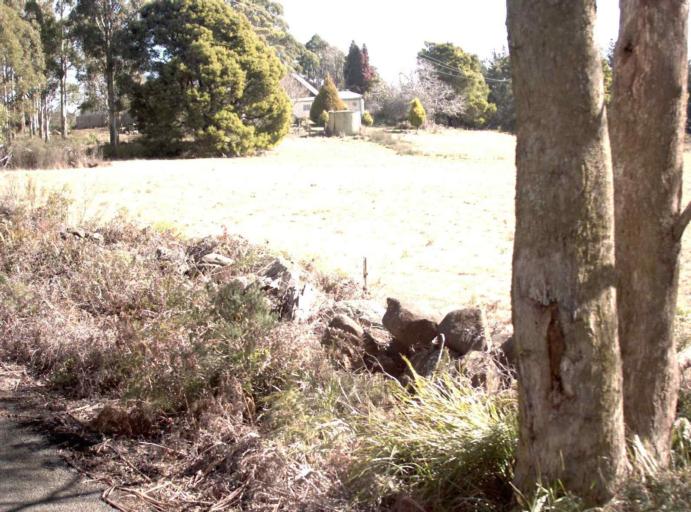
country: AU
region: Tasmania
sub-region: Launceston
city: Mayfield
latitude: -41.3109
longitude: 147.2043
